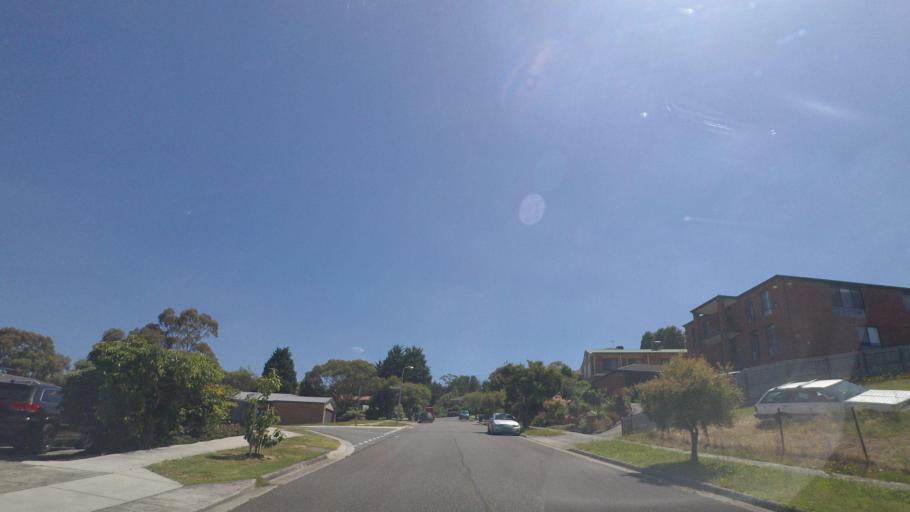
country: AU
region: Victoria
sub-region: Knox
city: Ferntree Gully
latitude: -37.8976
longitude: 145.2849
